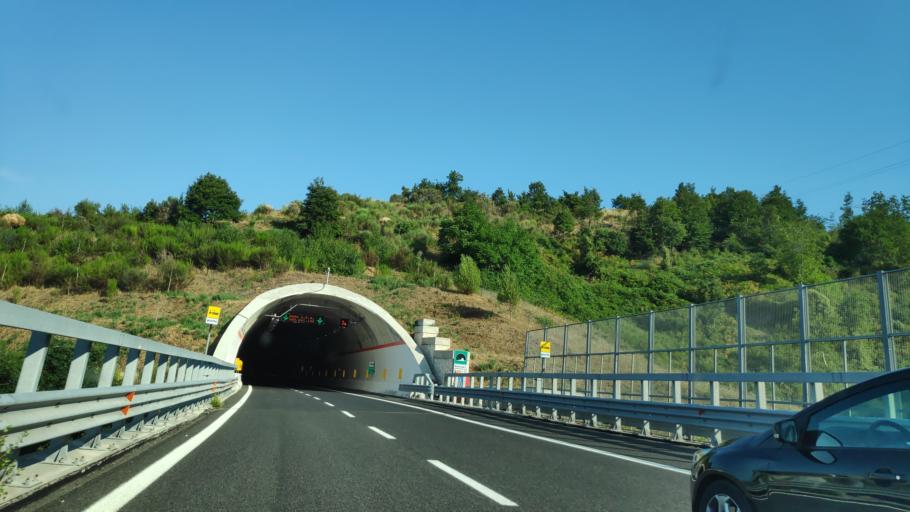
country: IT
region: Basilicate
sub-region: Provincia di Potenza
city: Lagonegro
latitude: 40.1106
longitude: 15.7920
